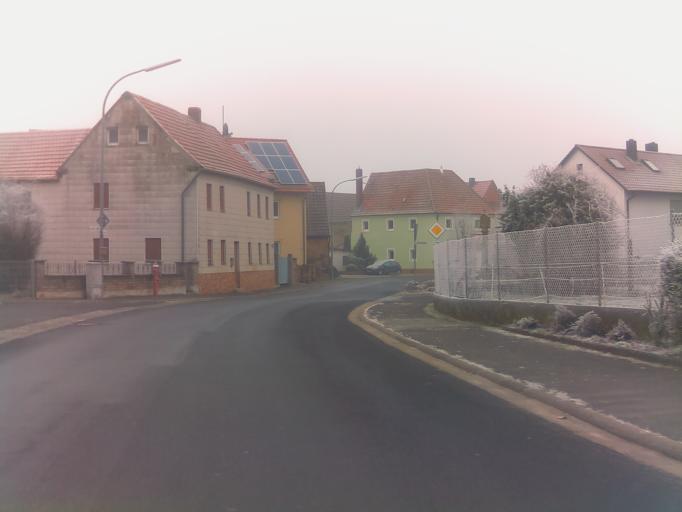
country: DE
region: Bavaria
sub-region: Regierungsbezirk Unterfranken
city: Lulsfeld
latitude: 49.8692
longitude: 10.3180
